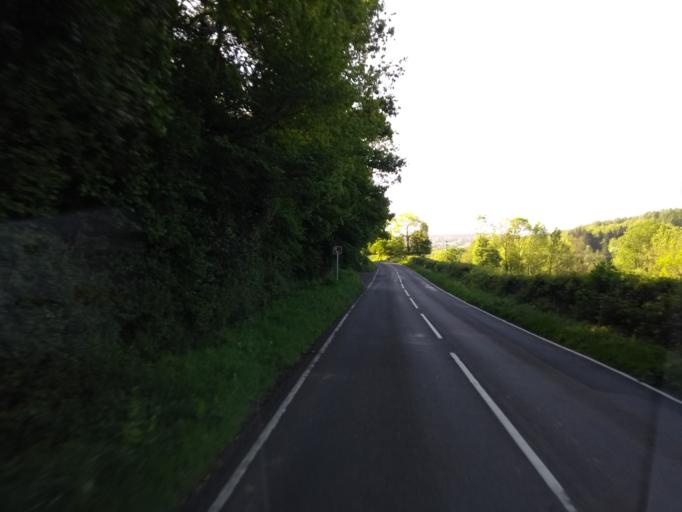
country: GB
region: England
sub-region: Somerset
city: Taunton
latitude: 50.9628
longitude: -3.0920
